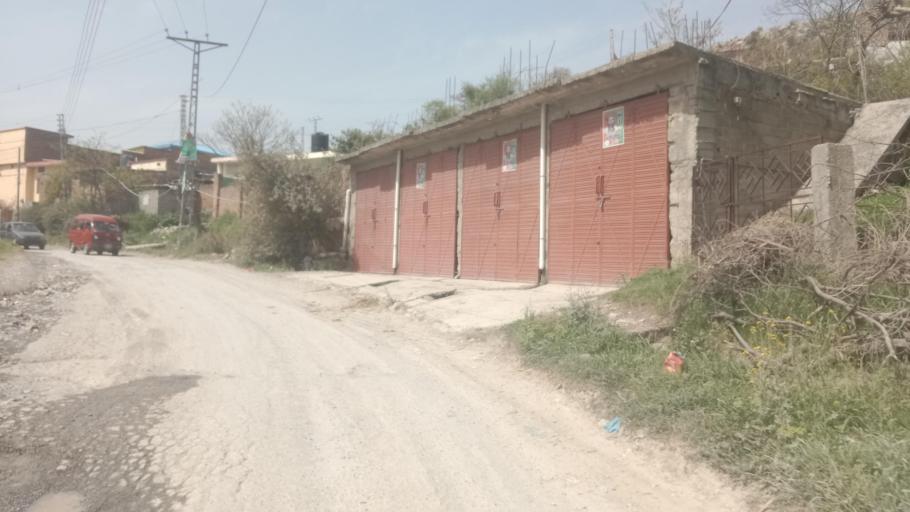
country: PK
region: Khyber Pakhtunkhwa
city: Abbottabad
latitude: 34.1673
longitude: 73.2812
